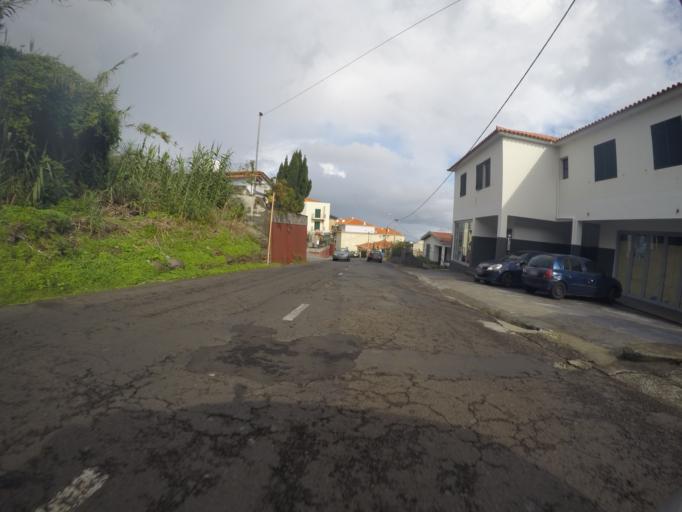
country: PT
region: Madeira
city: Canico
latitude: 32.6508
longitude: -16.8490
